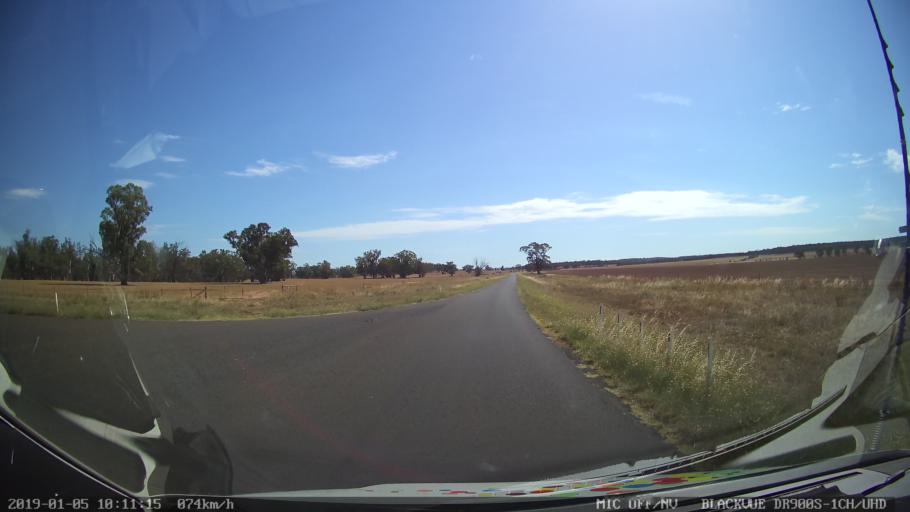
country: AU
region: New South Wales
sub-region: Gilgandra
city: Gilgandra
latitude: -31.6146
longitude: 148.8992
